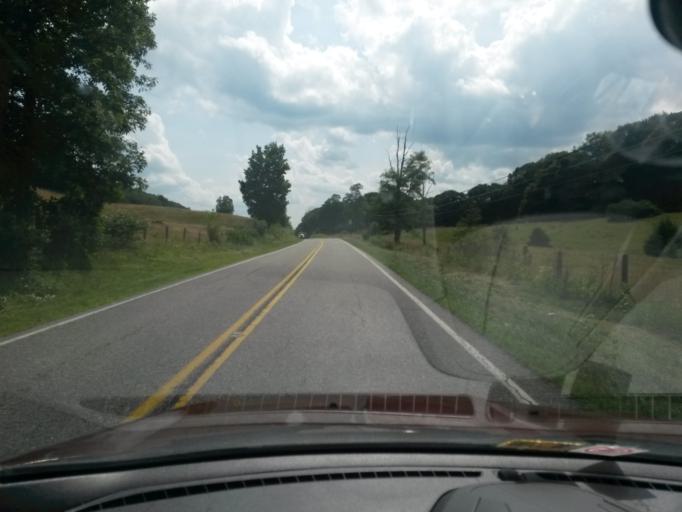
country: US
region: Virginia
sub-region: Highland County
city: Monterey
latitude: 38.4387
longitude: -79.5446
